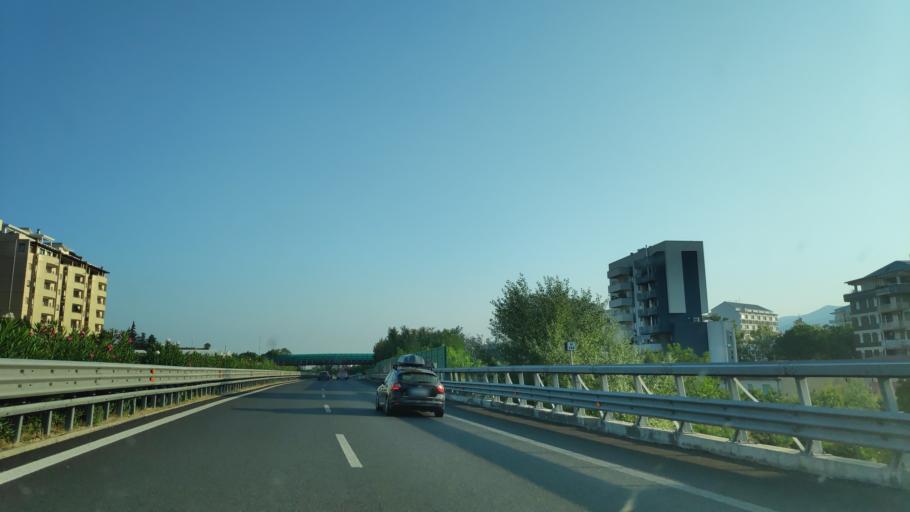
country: IT
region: Calabria
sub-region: Provincia di Cosenza
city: Quattromiglia
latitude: 39.3232
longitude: 16.2398
